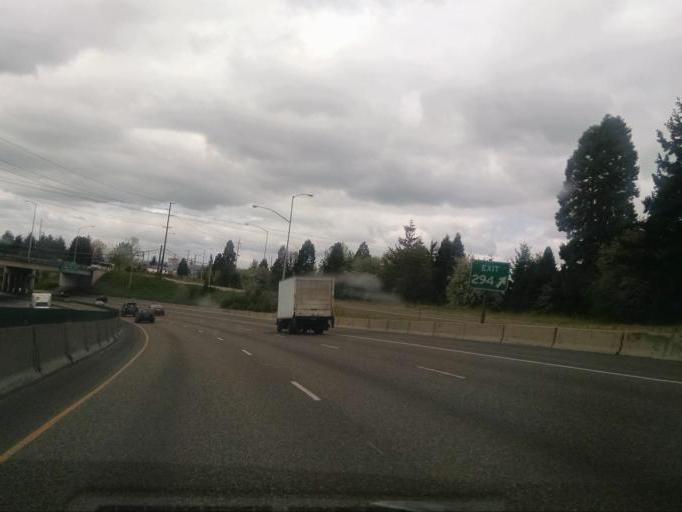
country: US
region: Oregon
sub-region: Washington County
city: Metzger
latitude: 45.4447
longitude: -122.7382
